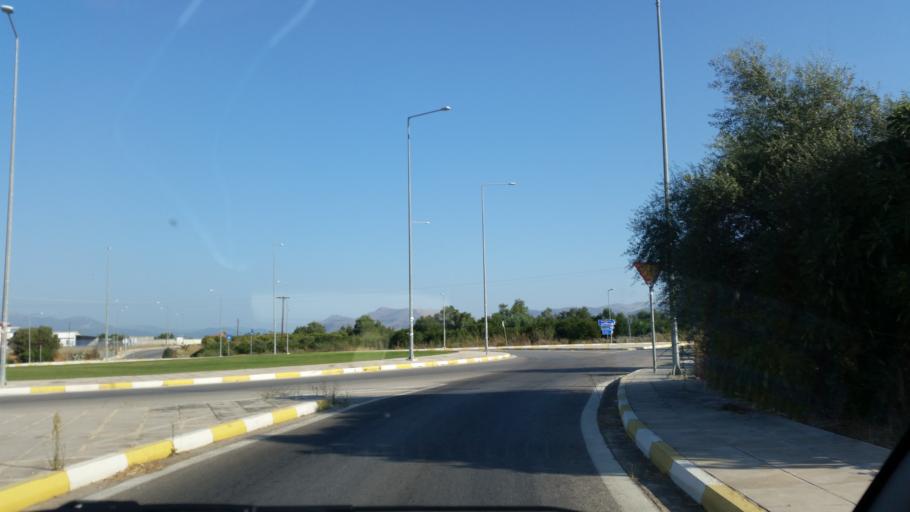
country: GR
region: Peloponnese
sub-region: Nomos Argolidos
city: Ayios Adhrianos
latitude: 37.5915
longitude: 22.8300
